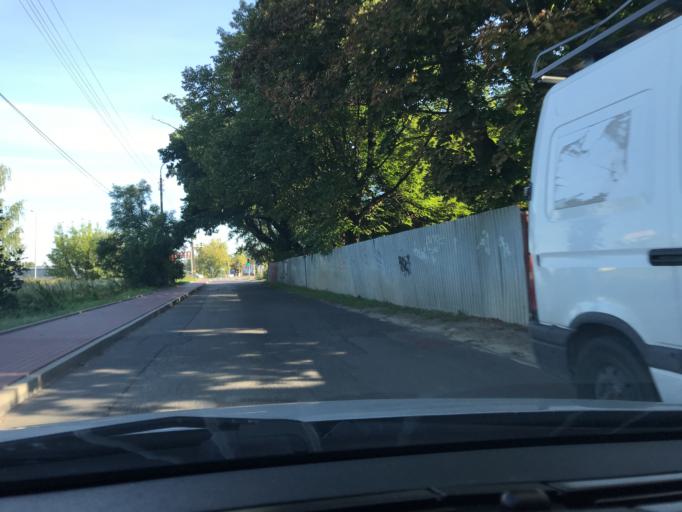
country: PL
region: Masovian Voivodeship
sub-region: Powiat pruszkowski
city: Piastow
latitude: 52.1720
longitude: 20.8404
